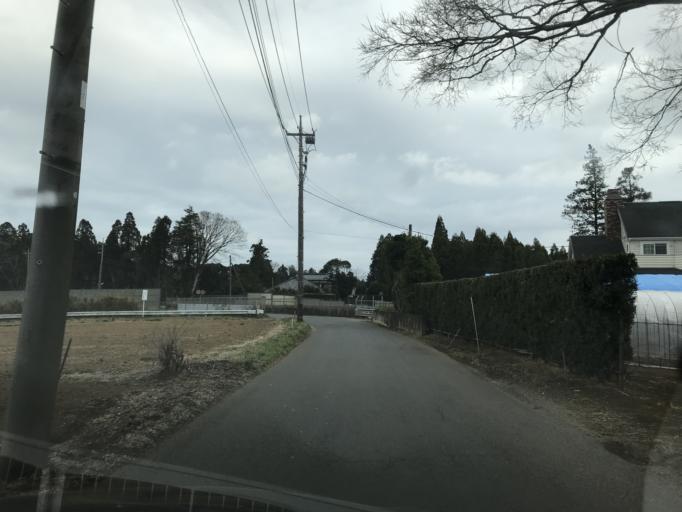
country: JP
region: Chiba
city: Sawara
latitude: 35.8421
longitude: 140.4891
